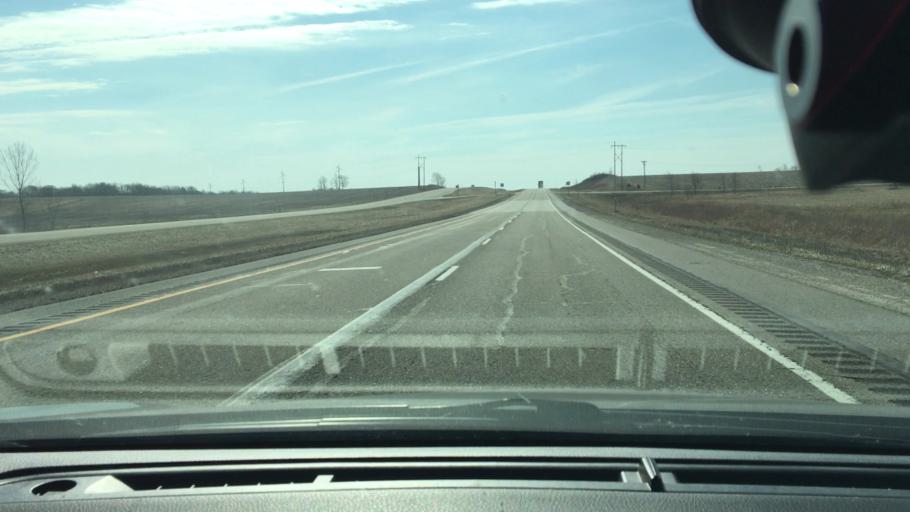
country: US
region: Iowa
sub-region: Floyd County
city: Charles City
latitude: 43.0035
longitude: -92.6154
